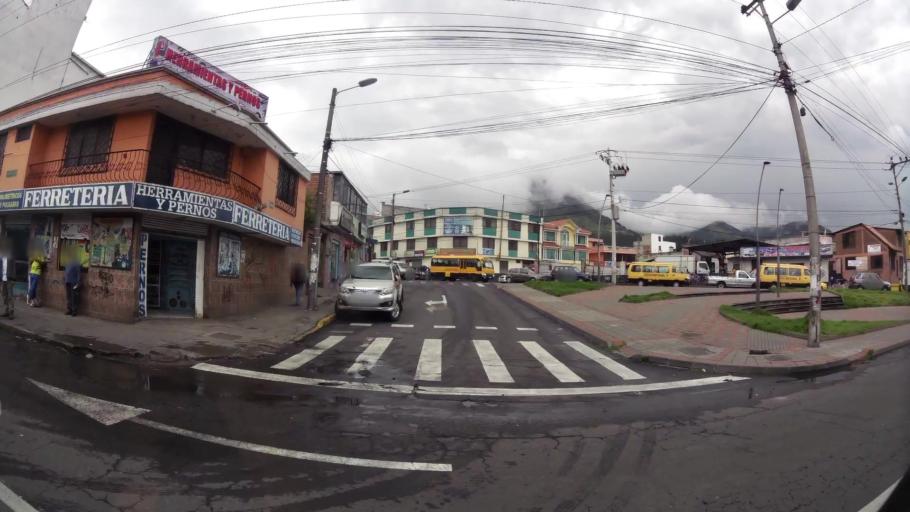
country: EC
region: Pichincha
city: Quito
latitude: -0.2610
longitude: -78.5468
